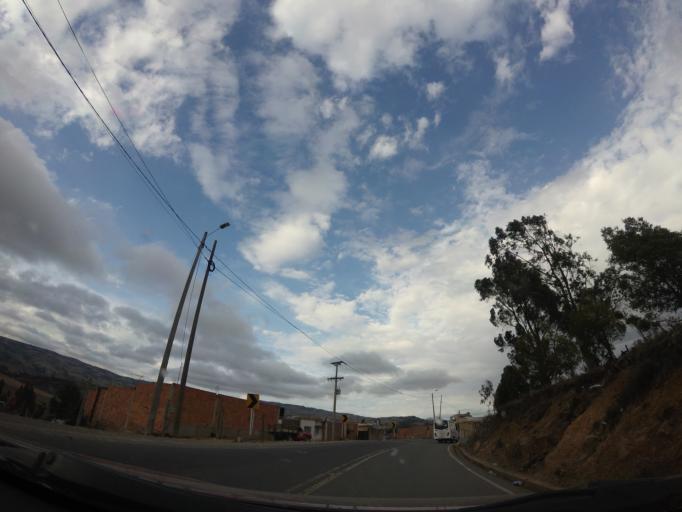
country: CO
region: Boyaca
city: Tunja
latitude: 5.5493
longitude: -73.3746
